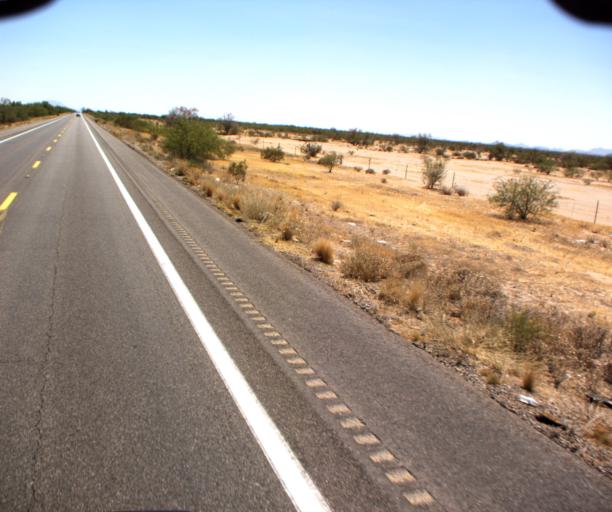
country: US
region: Arizona
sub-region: Pinal County
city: Gold Camp
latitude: 33.2045
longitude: -111.3482
